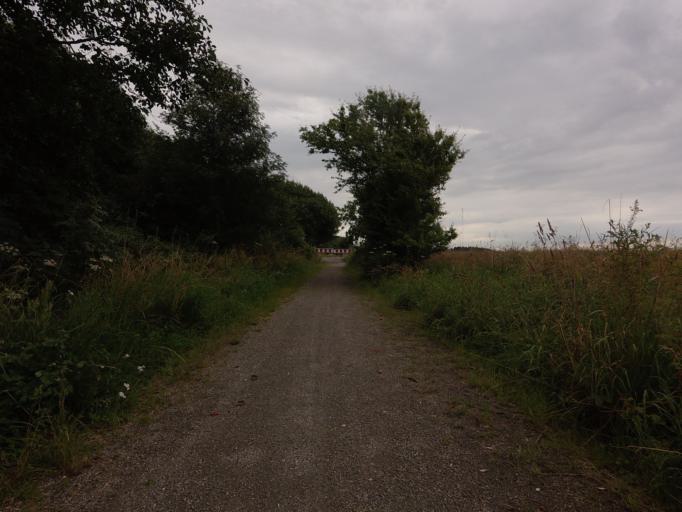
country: DK
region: North Denmark
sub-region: Alborg Kommune
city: Vadum
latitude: 57.1122
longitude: 9.8821
